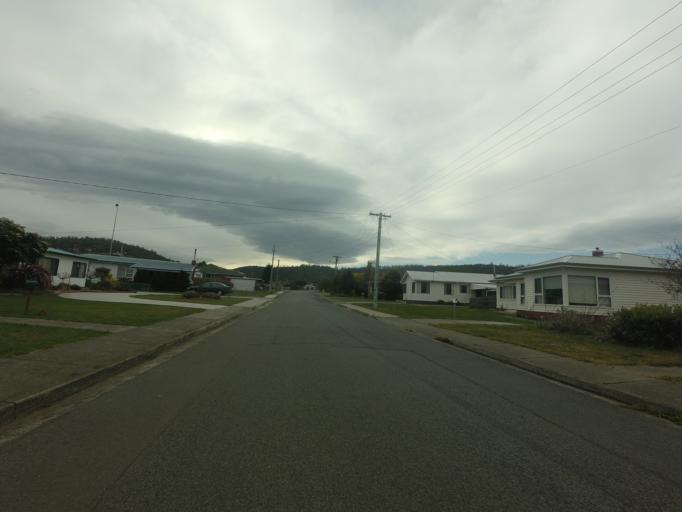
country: AU
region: Tasmania
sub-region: Clarence
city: Howrah
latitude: -42.8794
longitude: 147.3964
